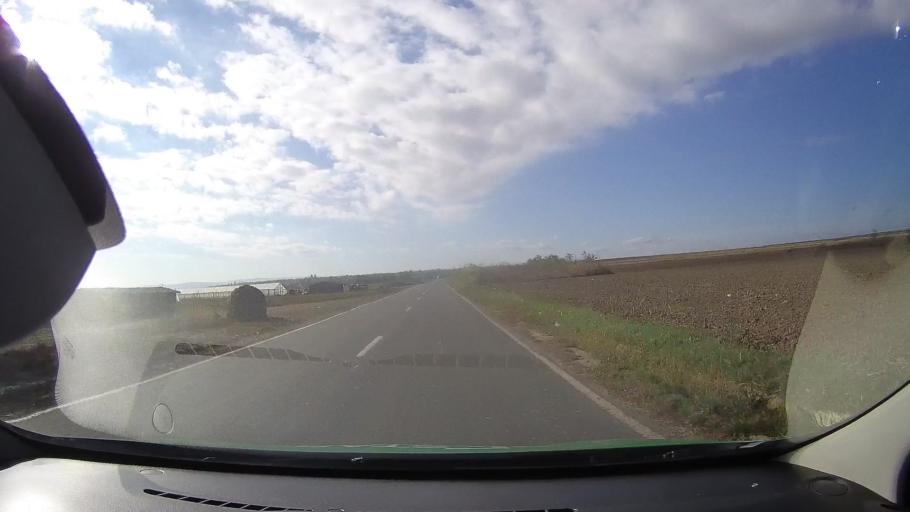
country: RO
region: Tulcea
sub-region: Comuna Sarichioi
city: Sarichioi
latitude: 44.9649
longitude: 28.8639
